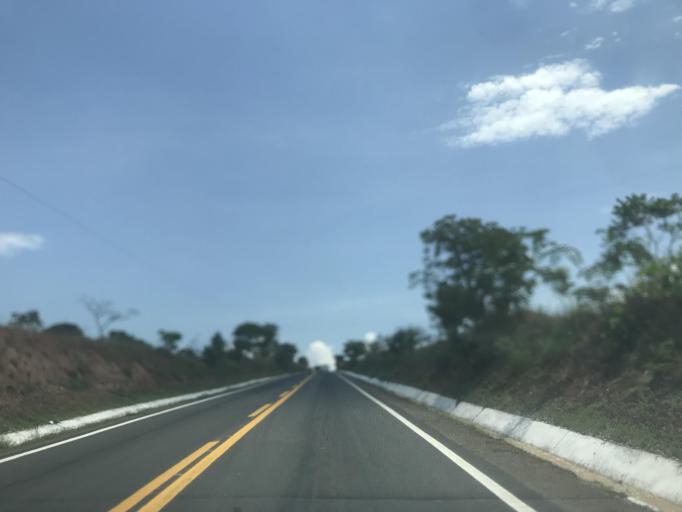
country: BR
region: Goias
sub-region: Bela Vista De Goias
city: Bela Vista de Goias
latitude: -17.1279
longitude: -48.6685
